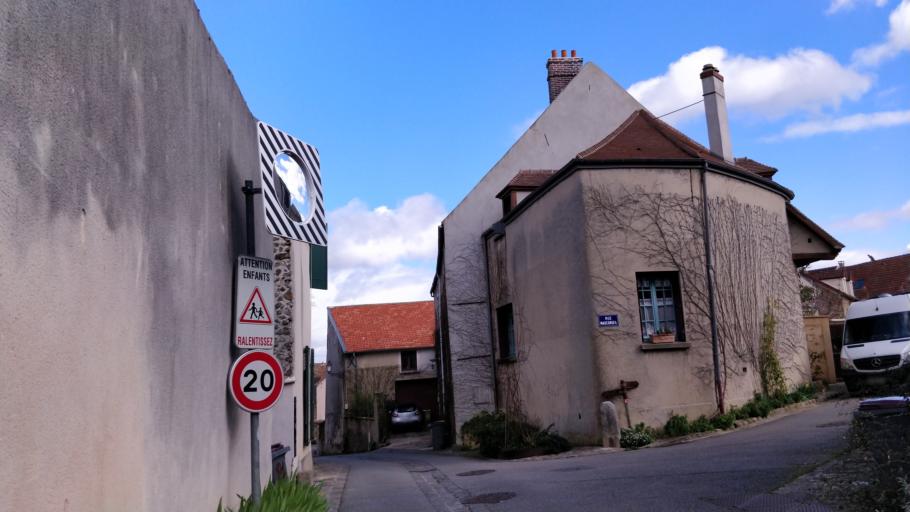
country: FR
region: Ile-de-France
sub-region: Departement de l'Essonne
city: Gometz-le-Chatel
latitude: 48.6782
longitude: 2.1380
